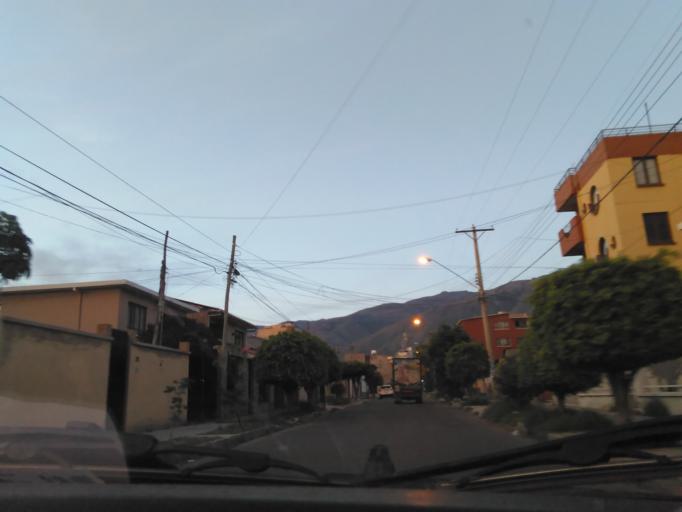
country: BO
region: Cochabamba
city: Cochabamba
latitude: -17.3756
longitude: -66.1658
